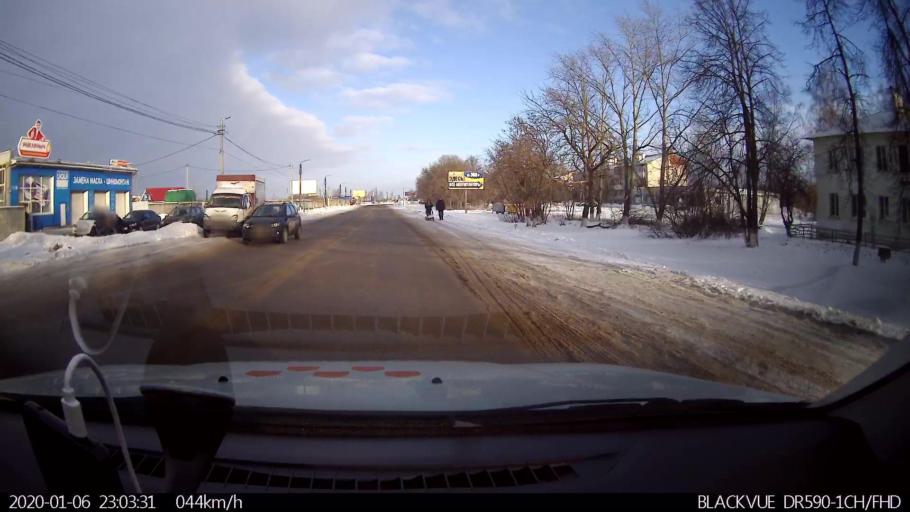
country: RU
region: Nizjnij Novgorod
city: Bogorodsk
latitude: 56.1132
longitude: 43.5347
